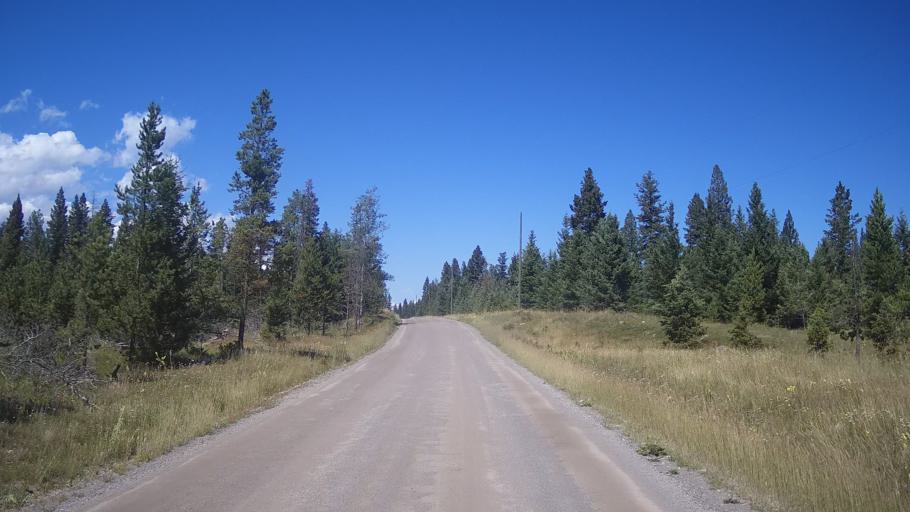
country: CA
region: British Columbia
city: Cache Creek
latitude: 51.2062
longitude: -121.5960
